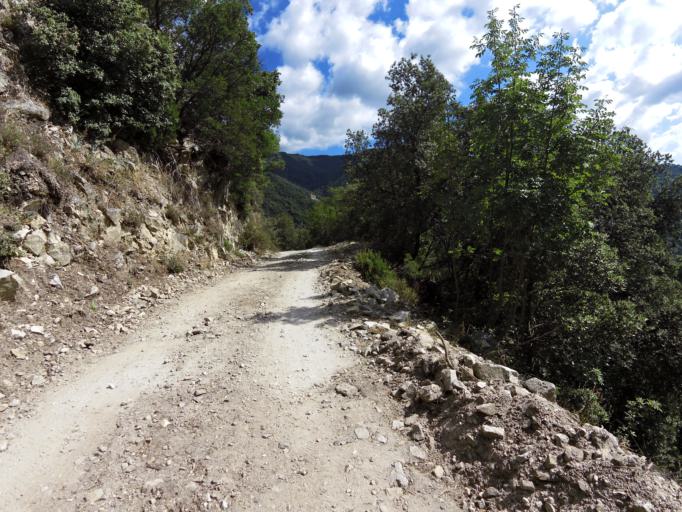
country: IT
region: Calabria
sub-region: Provincia di Reggio Calabria
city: Bivongi
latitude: 38.4915
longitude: 16.4058
